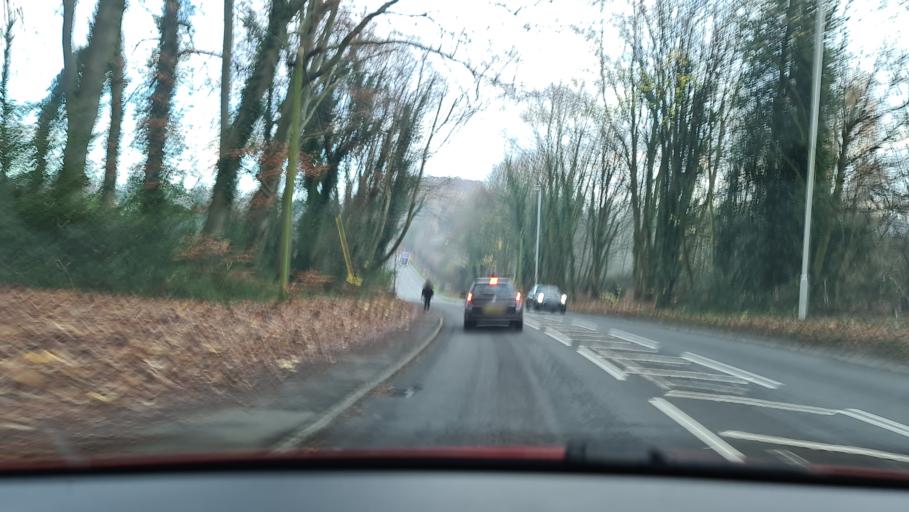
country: GB
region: England
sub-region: Buckinghamshire
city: Great Missenden
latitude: 51.6542
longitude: -0.7056
